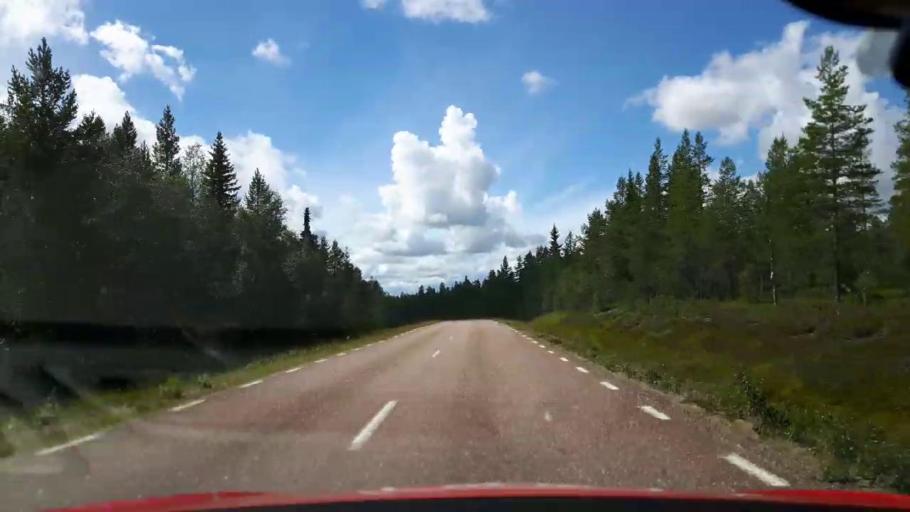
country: SE
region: Dalarna
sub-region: Alvdalens Kommun
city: AElvdalen
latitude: 61.8110
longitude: 13.5278
